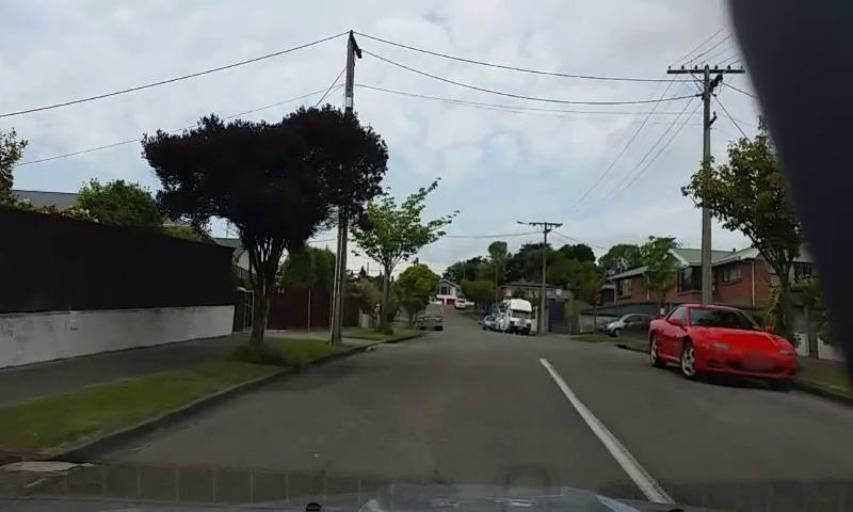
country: NZ
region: Canterbury
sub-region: Timaru District
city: Timaru
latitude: -44.3736
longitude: 171.2345
